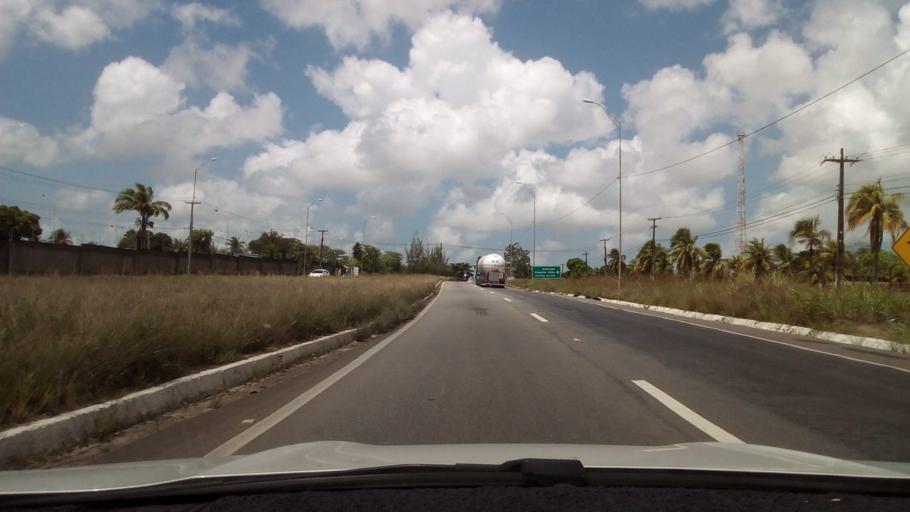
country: BR
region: Paraiba
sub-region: Conde
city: Conde
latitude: -7.2021
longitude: -34.9074
